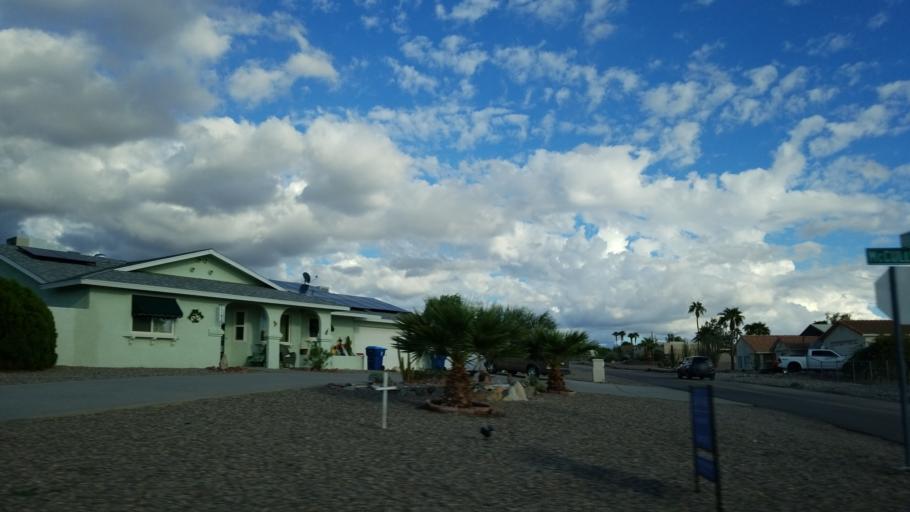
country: US
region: Arizona
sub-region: Mohave County
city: Lake Havasu City
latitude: 34.4583
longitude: -114.2590
